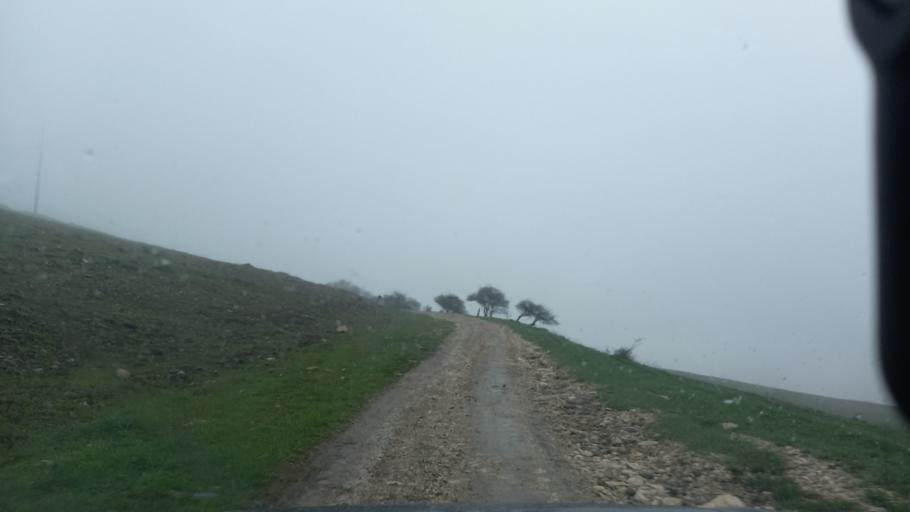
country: RU
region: Kabardino-Balkariya
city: Kamennomostskoye
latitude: 43.6719
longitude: 42.9778
